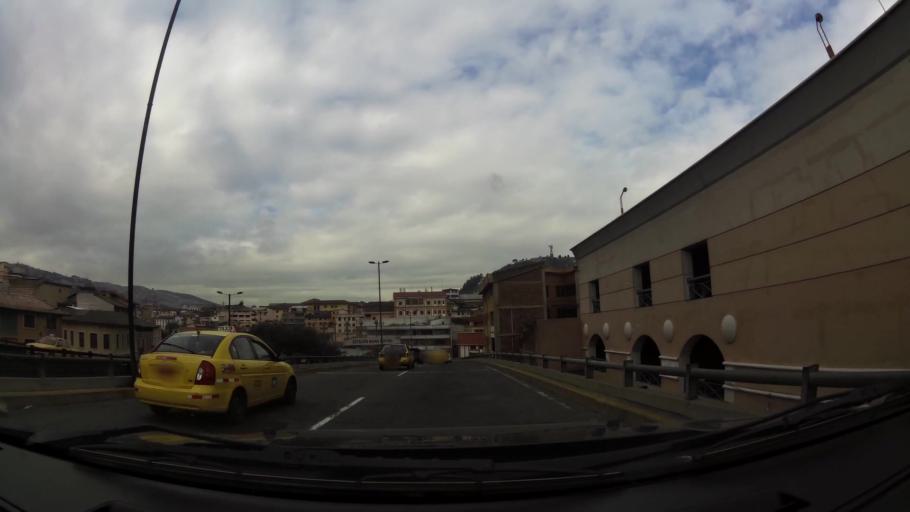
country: EC
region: Pichincha
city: Quito
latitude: -0.2208
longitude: -78.5081
